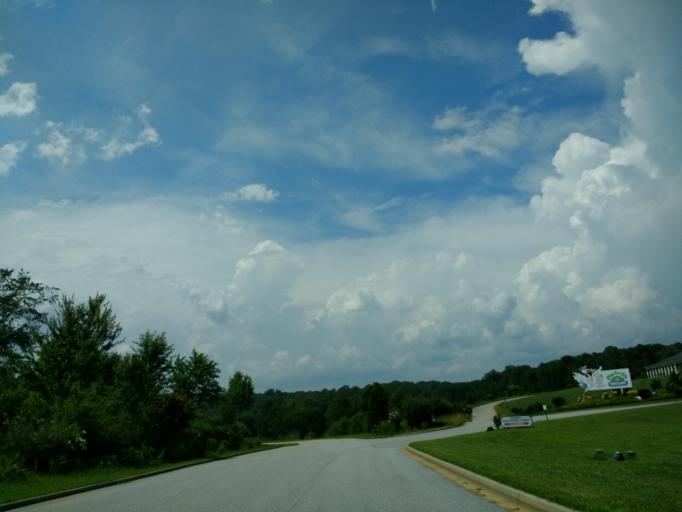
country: US
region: Georgia
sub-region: White County
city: Cleveland
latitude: 34.6204
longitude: -83.7629
